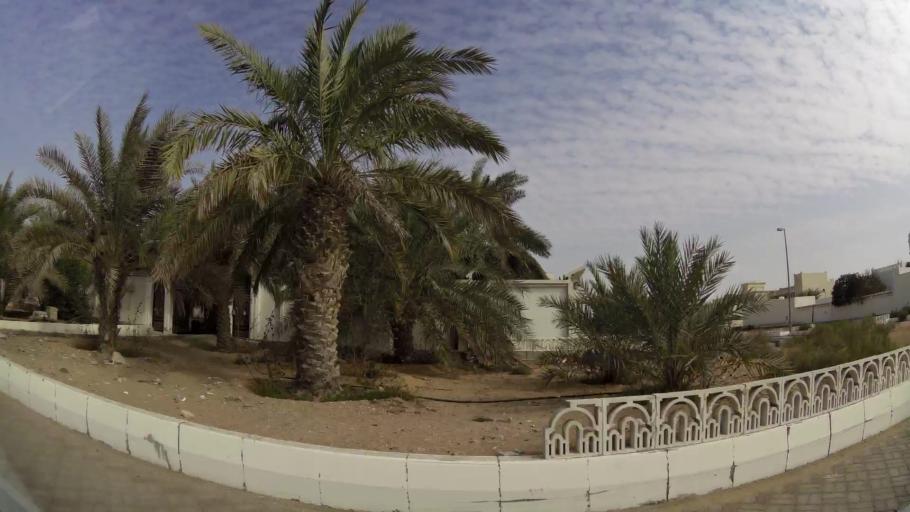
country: AE
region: Abu Dhabi
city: Abu Dhabi
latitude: 24.6051
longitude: 54.6989
